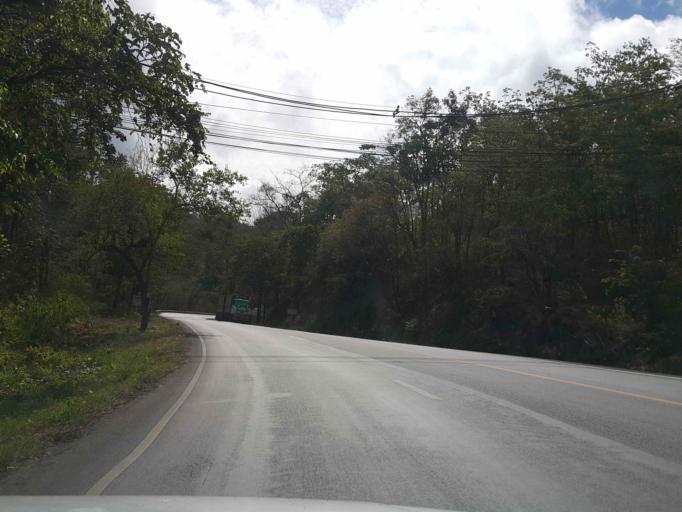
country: TH
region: Tak
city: Tak
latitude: 16.8099
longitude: 98.9865
